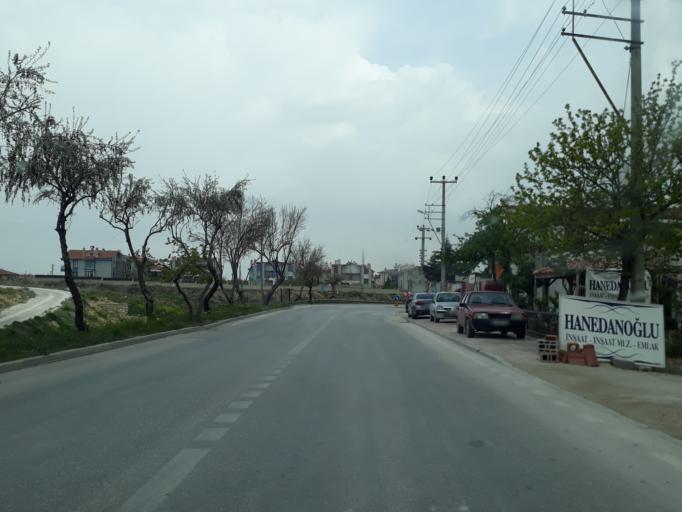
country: TR
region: Konya
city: Selcuklu
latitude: 37.9195
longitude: 32.4670
